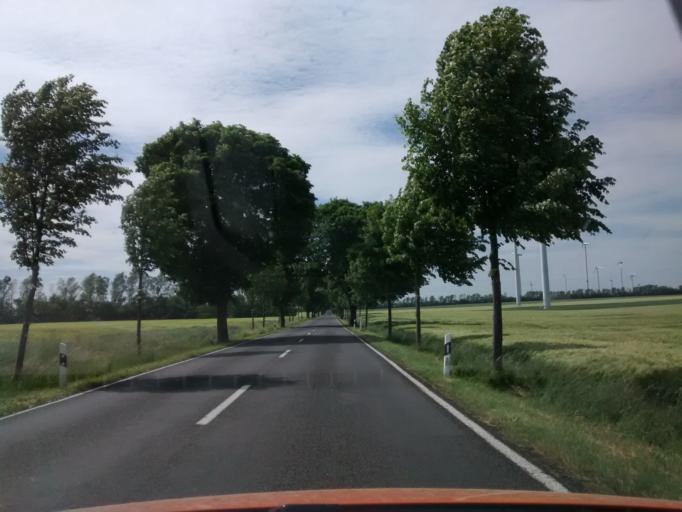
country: DE
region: Brandenburg
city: Ihlow
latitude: 51.8831
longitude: 13.3371
